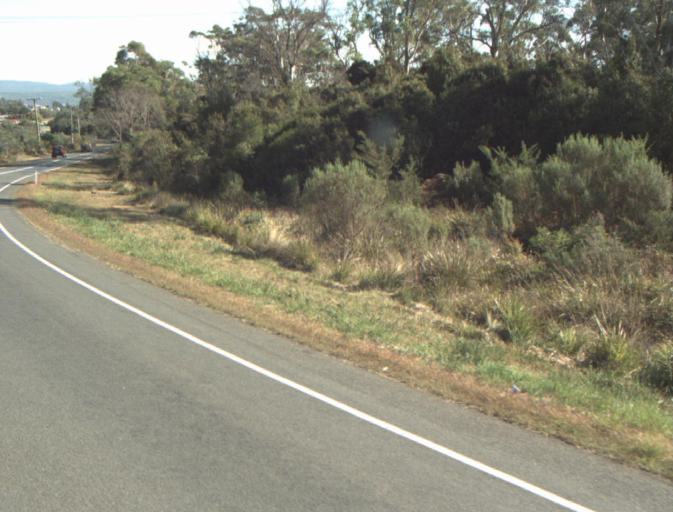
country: AU
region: Tasmania
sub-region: Launceston
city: Mayfield
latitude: -41.3648
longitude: 147.1449
